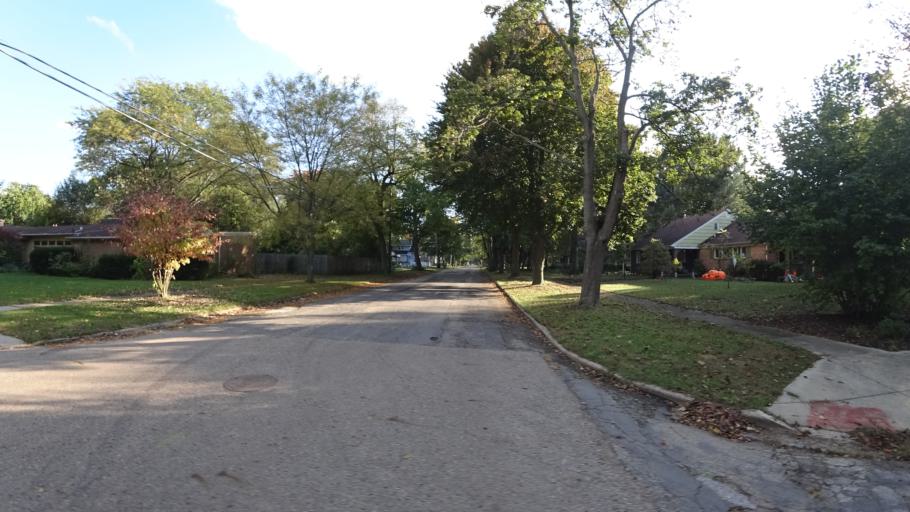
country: US
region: Michigan
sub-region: Saint Joseph County
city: Three Rivers
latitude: 41.9559
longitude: -85.6322
